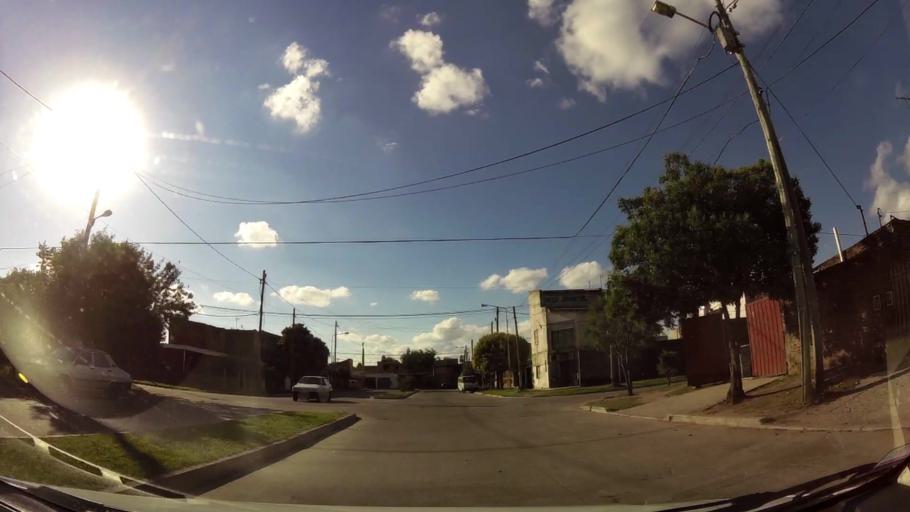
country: AR
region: Buenos Aires
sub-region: Partido de Moron
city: Moron
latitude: -34.6834
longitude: -58.6062
